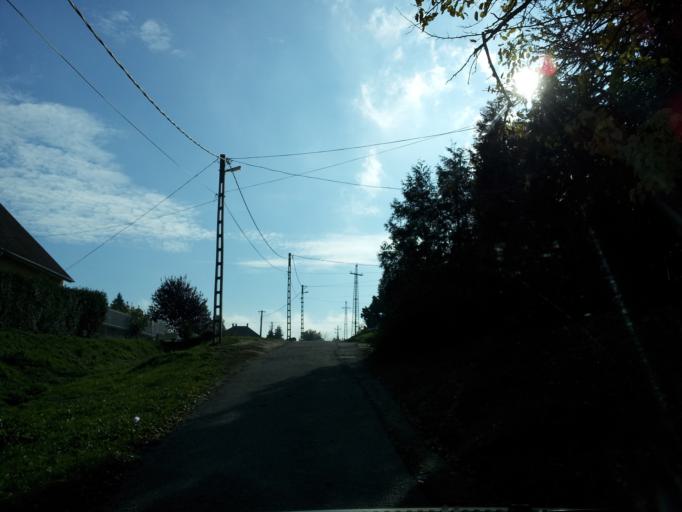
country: HU
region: Gyor-Moson-Sopron
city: Bakonyszentlaszlo
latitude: 47.3828
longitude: 17.8023
